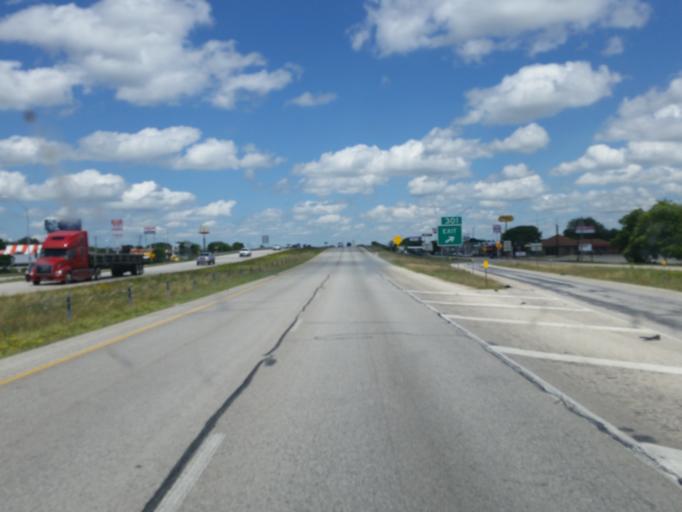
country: US
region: Texas
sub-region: Callahan County
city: Clyde
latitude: 32.4125
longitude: -99.4935
